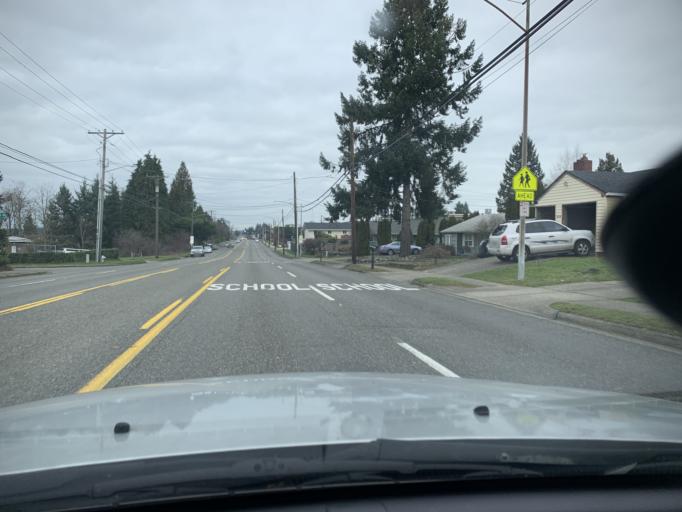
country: US
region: Washington
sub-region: Pierce County
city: University Place
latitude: 47.2523
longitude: -122.5369
